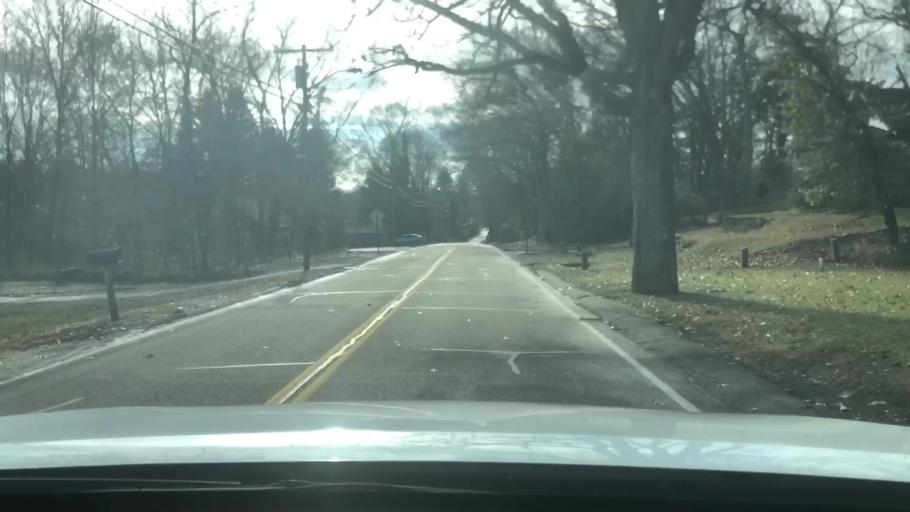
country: US
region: Massachusetts
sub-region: Worcester County
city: Blackstone
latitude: 42.0246
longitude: -71.5251
